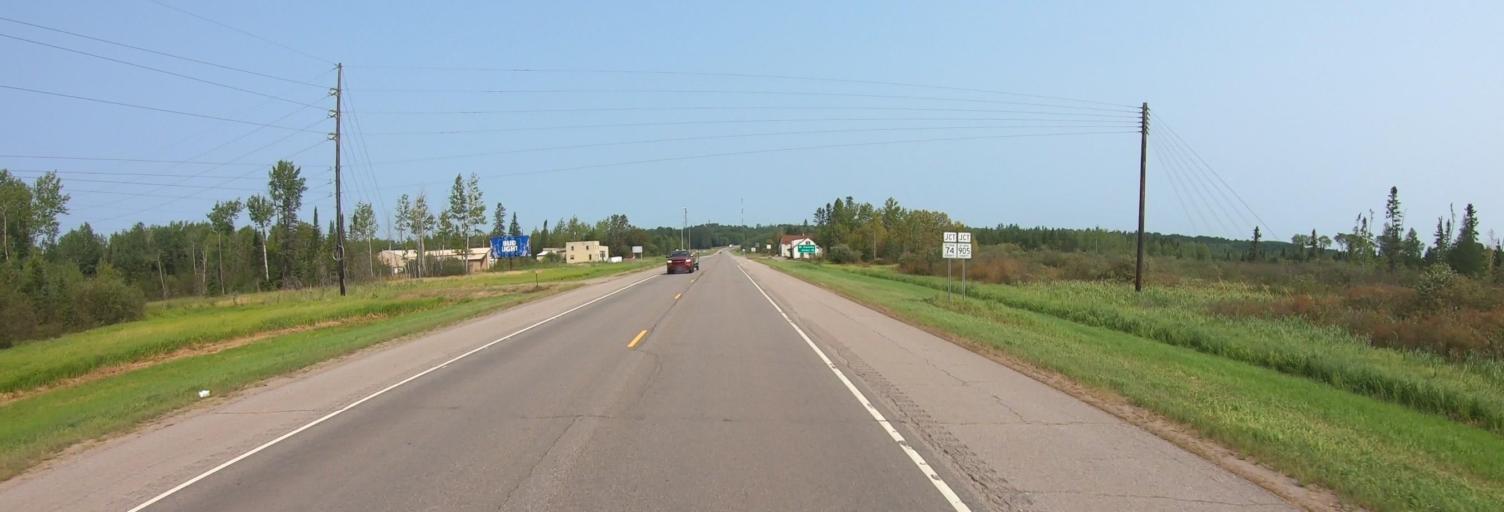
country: US
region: Minnesota
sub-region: Saint Louis County
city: Chisholm
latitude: 47.9615
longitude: -92.8293
